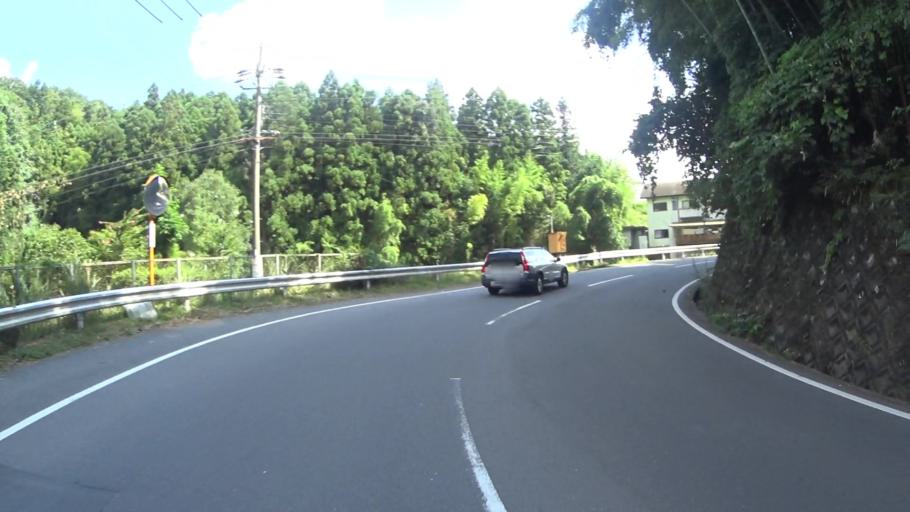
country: JP
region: Kyoto
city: Tanabe
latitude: 34.7607
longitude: 135.7410
